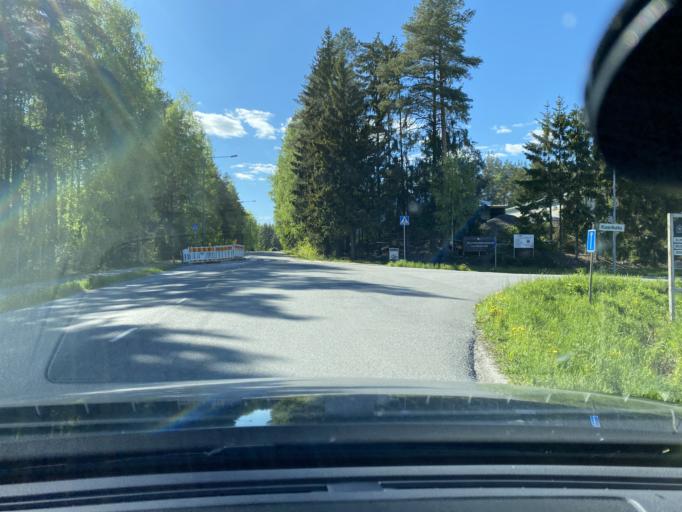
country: FI
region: Varsinais-Suomi
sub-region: Turku
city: Kaarina
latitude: 60.4182
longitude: 22.3386
